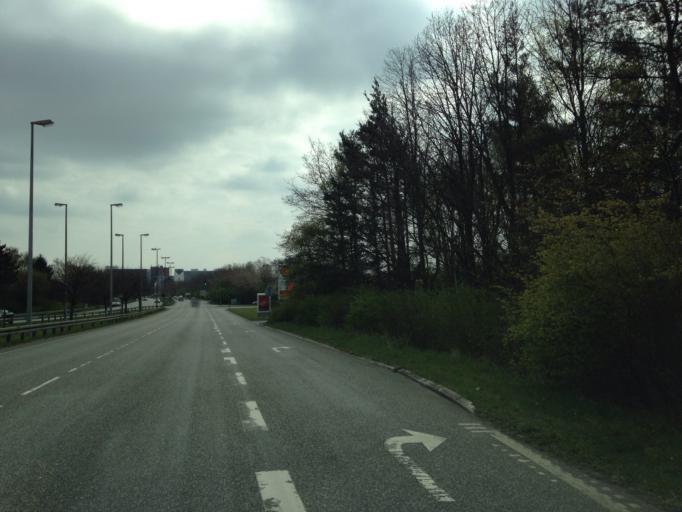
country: DK
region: Capital Region
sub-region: Ishoj Kommune
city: Ishoj
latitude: 55.6186
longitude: 12.3446
